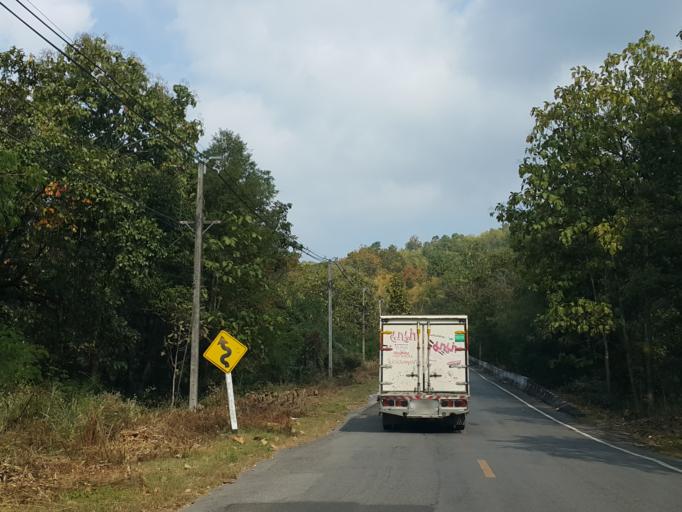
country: TH
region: Chiang Mai
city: Mae On
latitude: 18.8244
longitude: 99.2596
